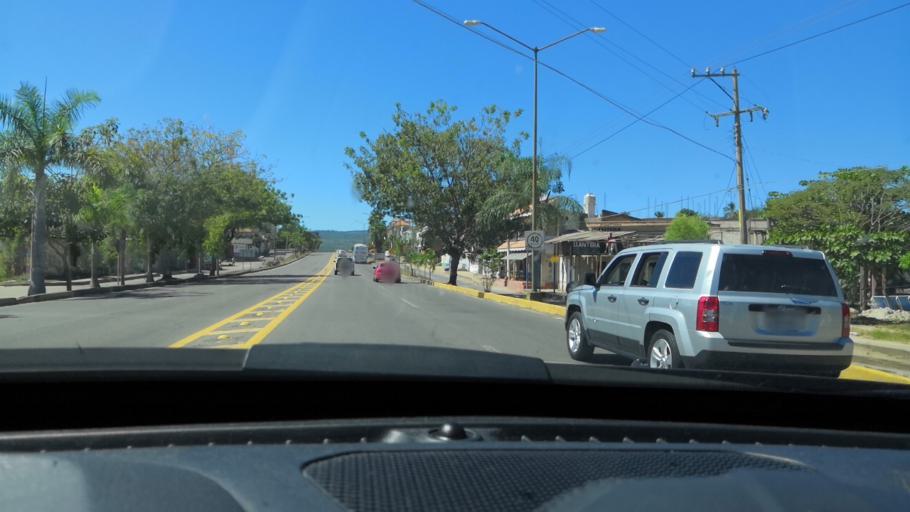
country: MX
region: Nayarit
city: Las Varas
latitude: 21.1773
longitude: -105.1403
